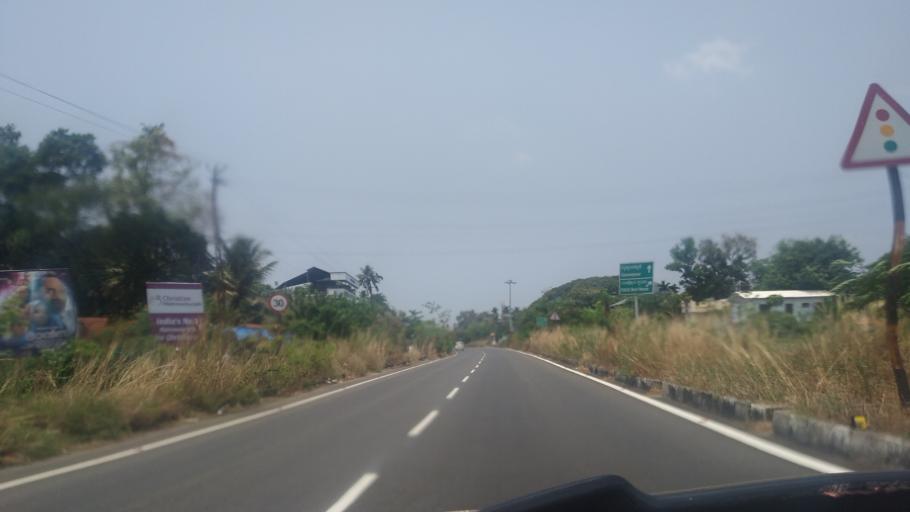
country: IN
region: Kerala
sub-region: Thrissur District
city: Kodungallur
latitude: 10.2249
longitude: 76.1959
